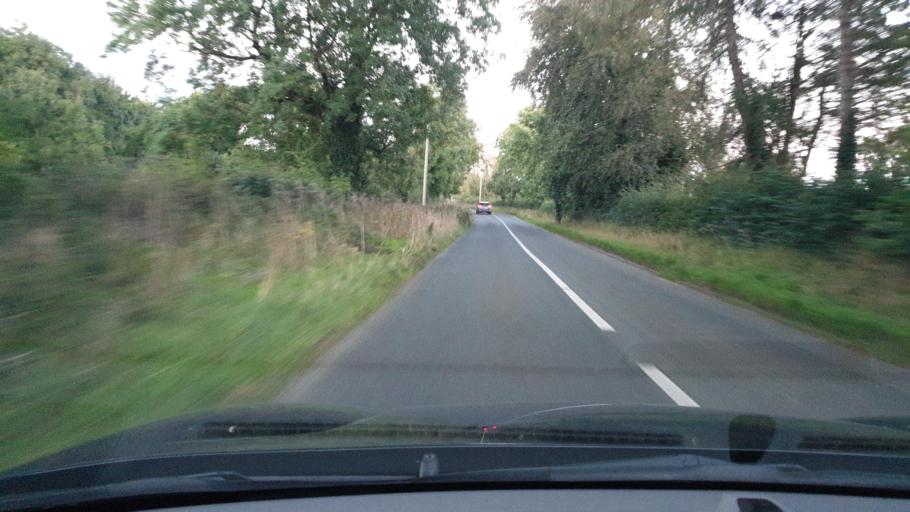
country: IE
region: Leinster
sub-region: Kildare
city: Clane
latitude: 53.3466
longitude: -6.6835
